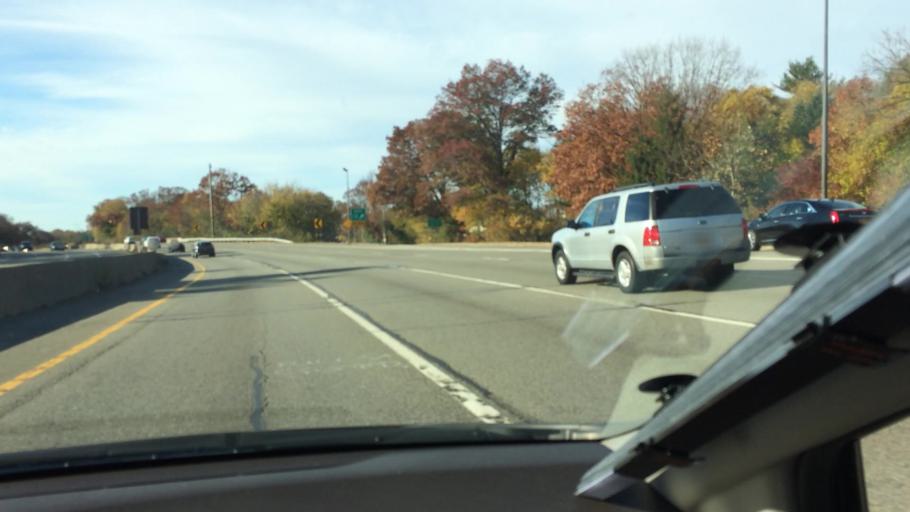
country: US
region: New York
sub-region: Nassau County
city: North Valley Stream
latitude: 40.6863
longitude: -73.7133
